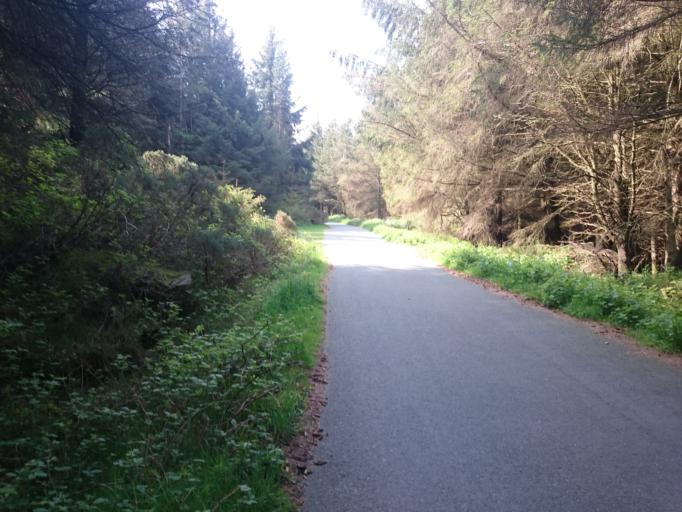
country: IE
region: Leinster
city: Balally
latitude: 53.2535
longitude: -6.2432
